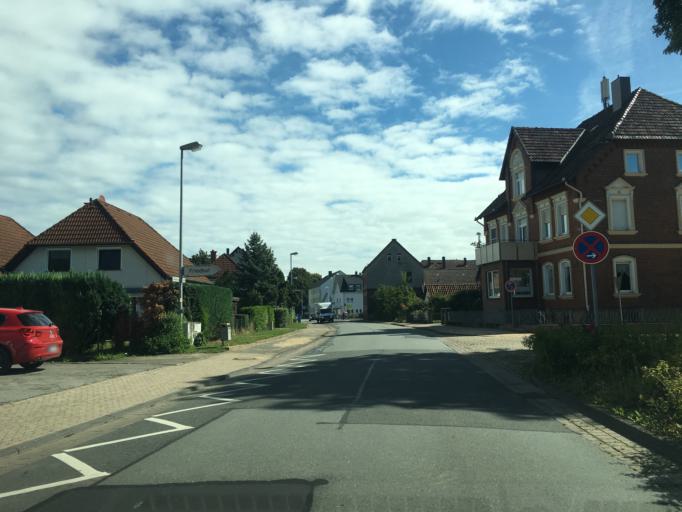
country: DE
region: Lower Saxony
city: Hameln
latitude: 52.0786
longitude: 9.3412
